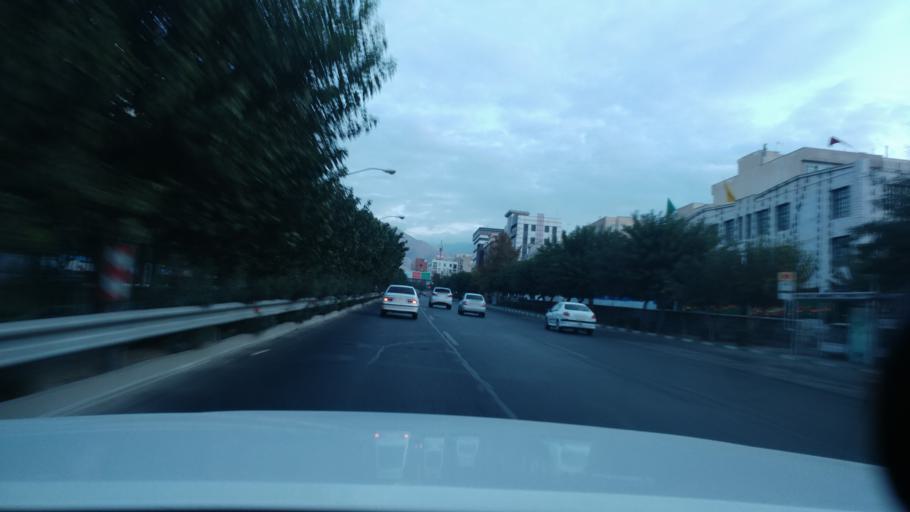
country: IR
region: Tehran
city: Tehran
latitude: 35.7391
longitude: 51.3135
